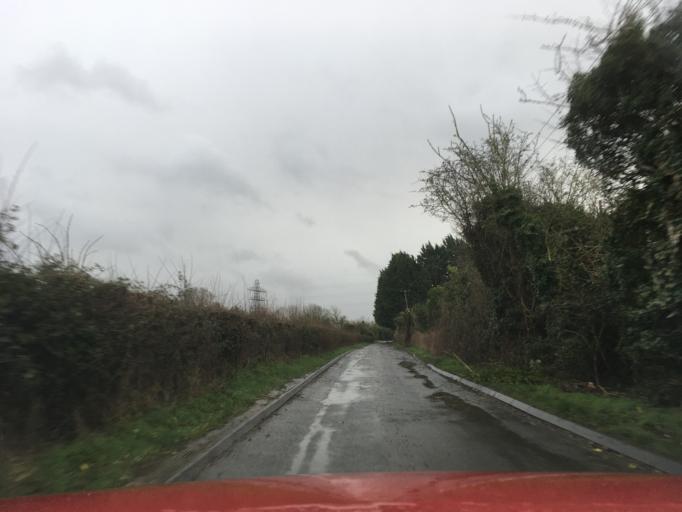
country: GB
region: England
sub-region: Oxfordshire
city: Oxford
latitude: 51.7576
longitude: -1.2842
